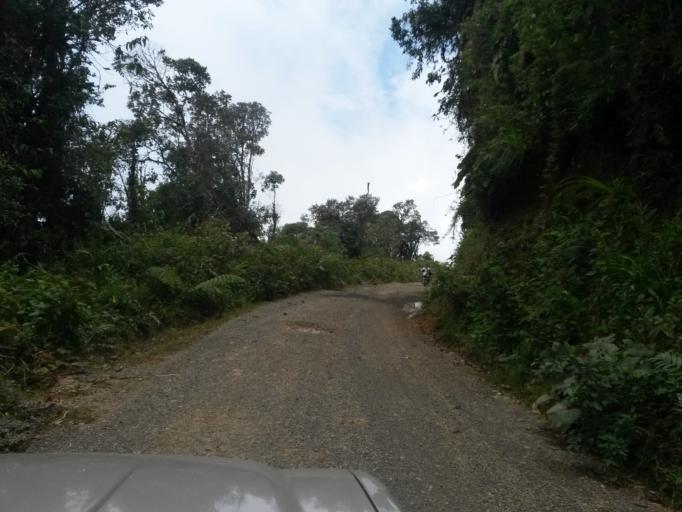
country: CO
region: Cauca
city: Villa Rica
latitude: 2.6685
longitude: -76.9048
